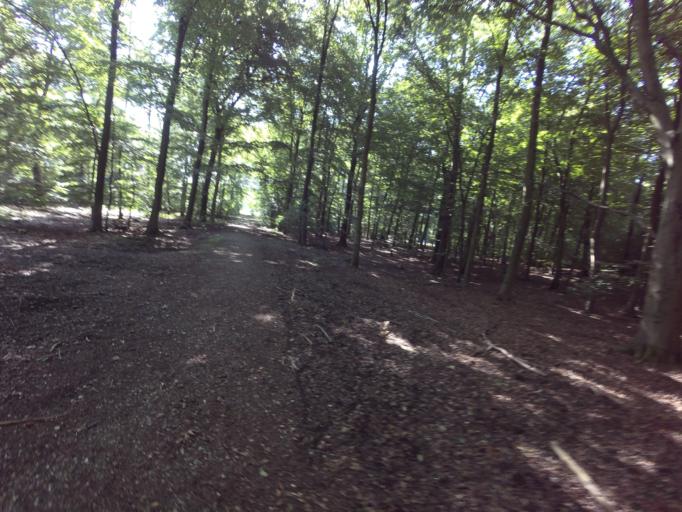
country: DE
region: North Rhine-Westphalia
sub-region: Regierungsbezirk Koln
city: Wassenberg
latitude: 51.1553
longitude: 6.1596
